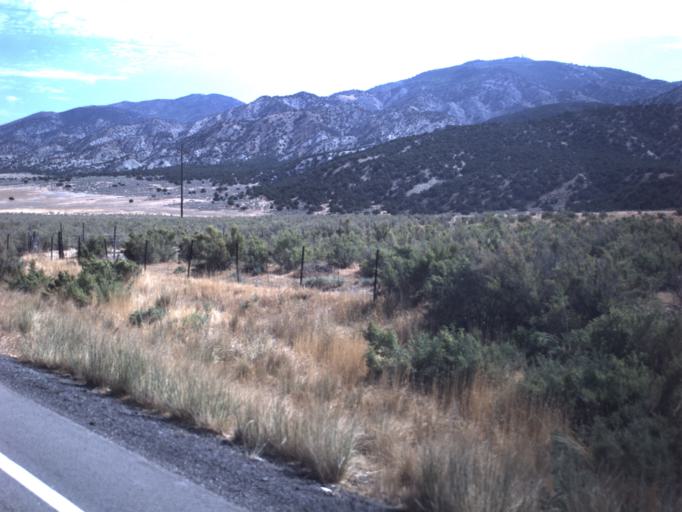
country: US
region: Utah
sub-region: Juab County
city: Nephi
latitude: 39.4807
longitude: -111.8894
